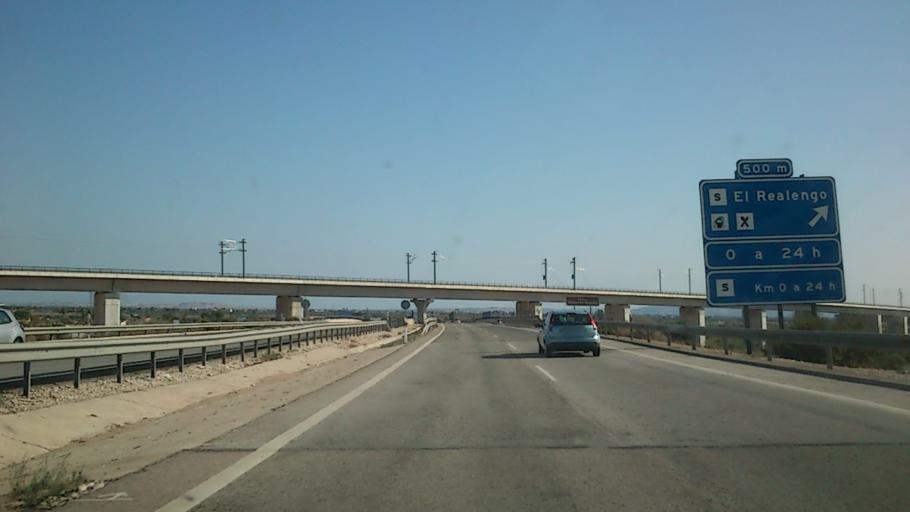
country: ES
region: Valencia
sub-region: Provincia de Alicante
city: San Isidro
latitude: 38.2043
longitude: -0.8167
